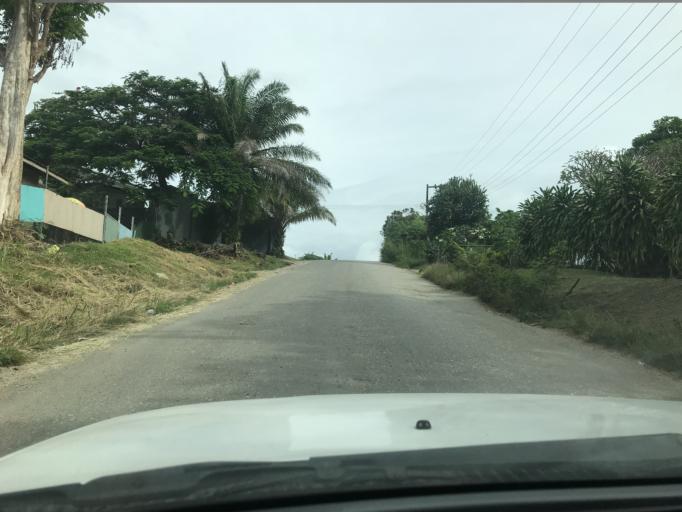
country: SB
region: Guadalcanal
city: Honiara
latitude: -9.4358
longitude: 159.9452
